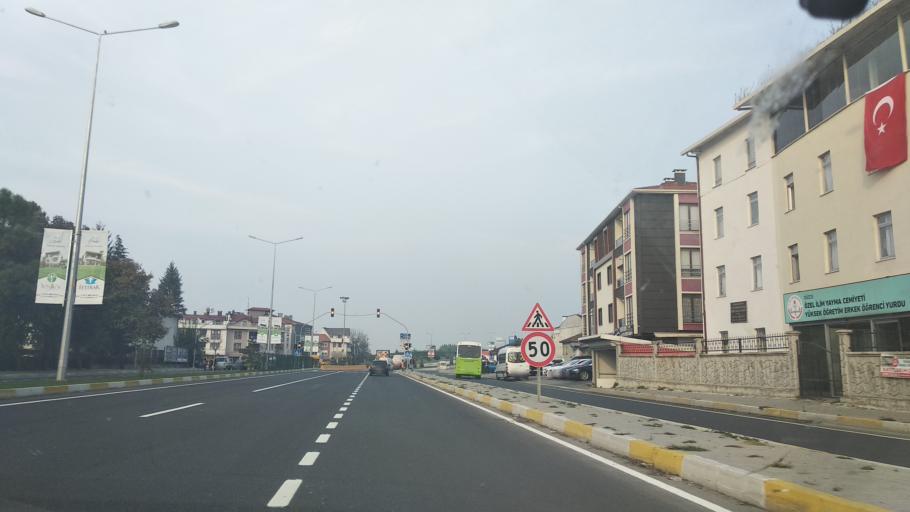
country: TR
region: Duzce
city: Duzce
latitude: 40.8346
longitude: 31.1703
